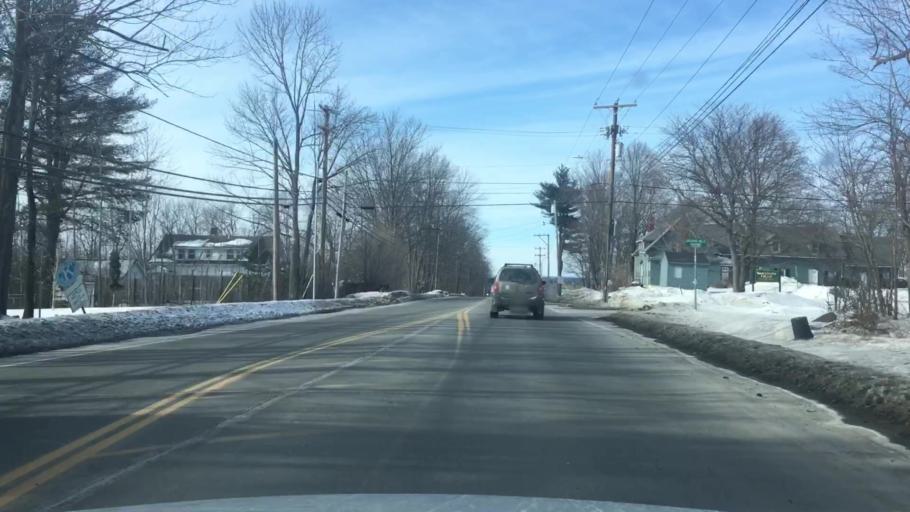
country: US
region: Maine
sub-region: Penobscot County
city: Bangor
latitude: 44.8316
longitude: -68.7871
